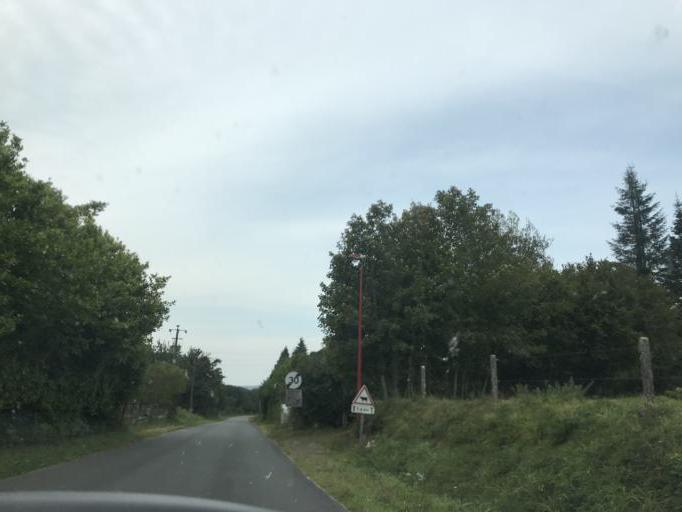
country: FR
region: Brittany
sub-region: Departement du Finistere
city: Plouneour-Menez
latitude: 48.3632
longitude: -3.8508
